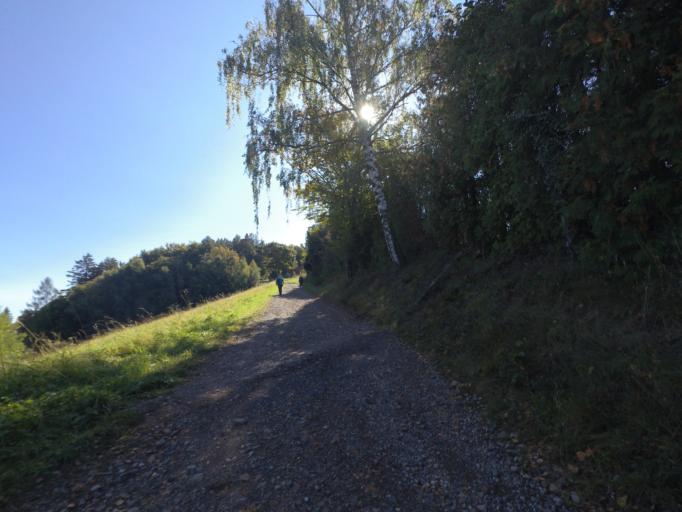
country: AT
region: Styria
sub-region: Politischer Bezirk Leibnitz
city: Kitzeck im Sausal
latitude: 46.7882
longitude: 15.4269
